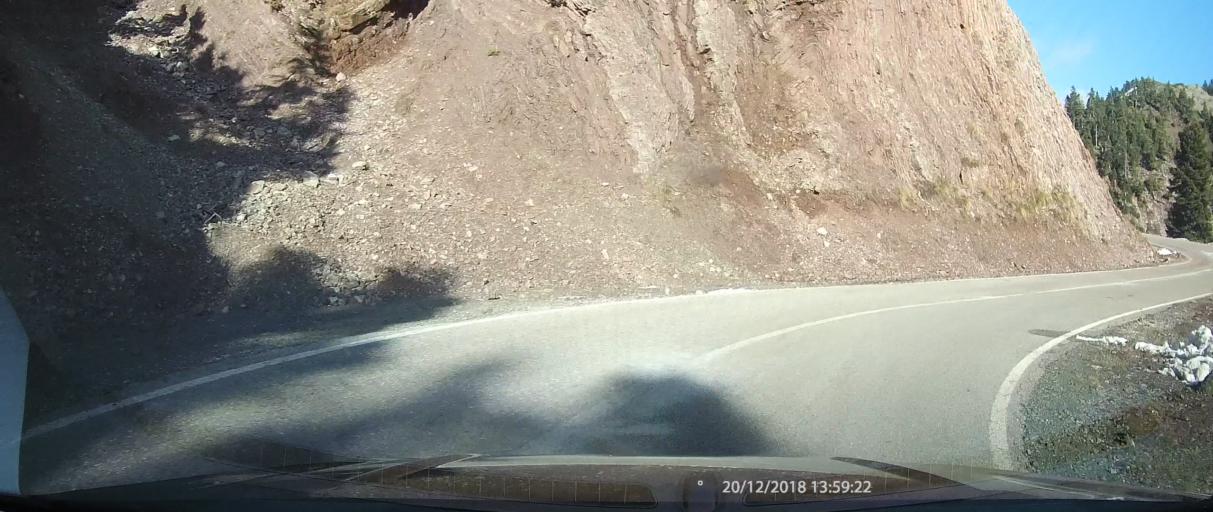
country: GR
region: West Greece
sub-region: Nomos Aitolias kai Akarnanias
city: Thermo
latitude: 38.7187
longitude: 21.6232
